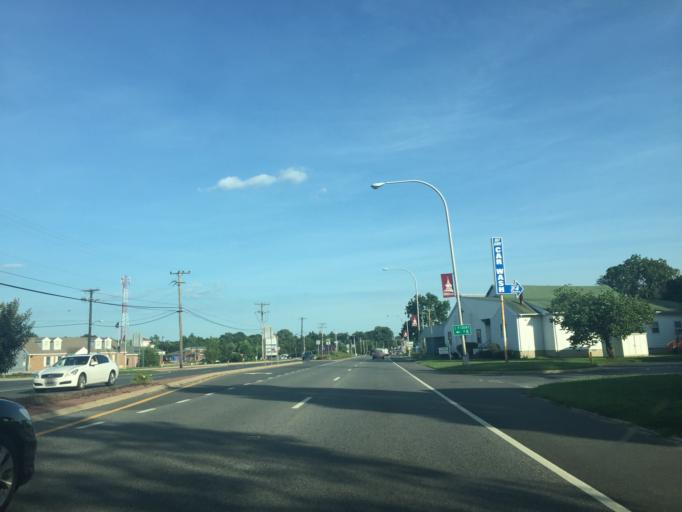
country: US
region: Delaware
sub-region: Kent County
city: Smyrna
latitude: 39.3008
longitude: -75.6025
